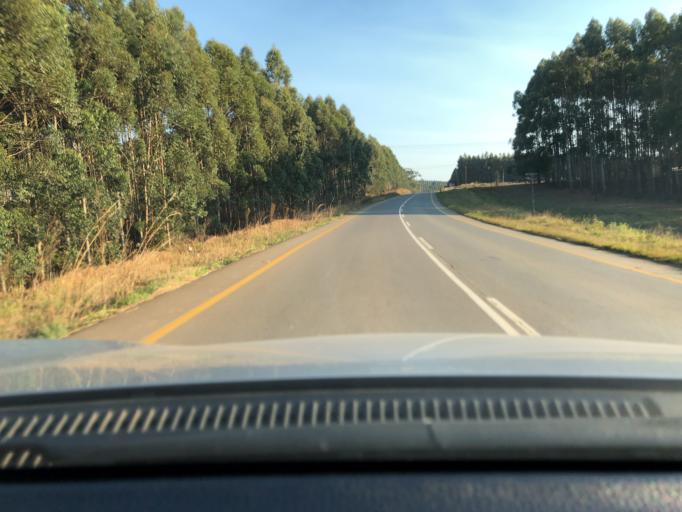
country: ZA
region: KwaZulu-Natal
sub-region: Sisonke District Municipality
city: Ixopo
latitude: -30.1807
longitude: 30.0595
